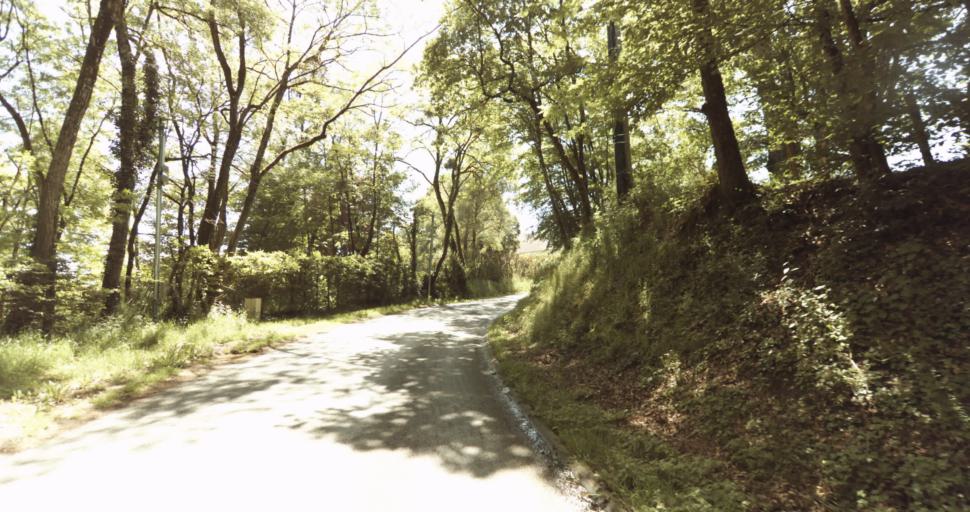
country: FR
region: Limousin
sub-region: Departement de la Haute-Vienne
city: Condat-sur-Vienne
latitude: 45.7889
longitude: 1.2988
